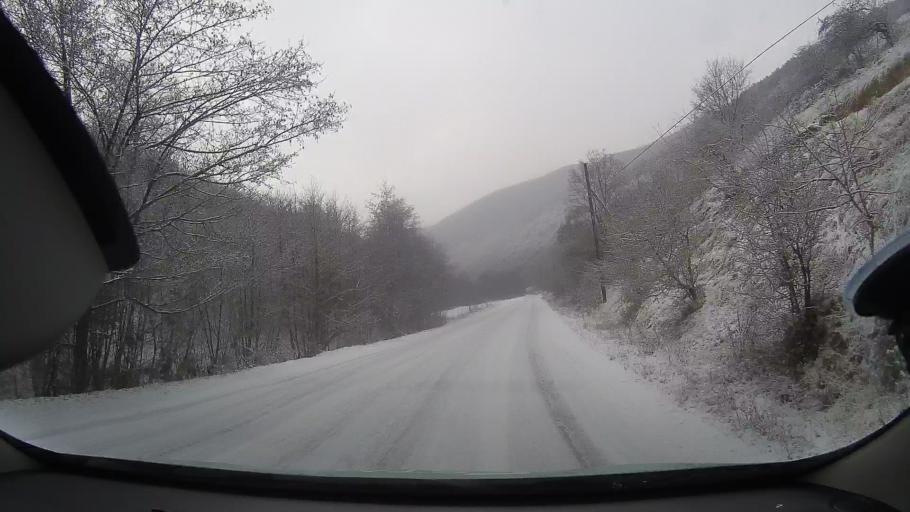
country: RO
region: Alba
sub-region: Comuna Rimetea
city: Rimetea
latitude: 46.4985
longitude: 23.5876
